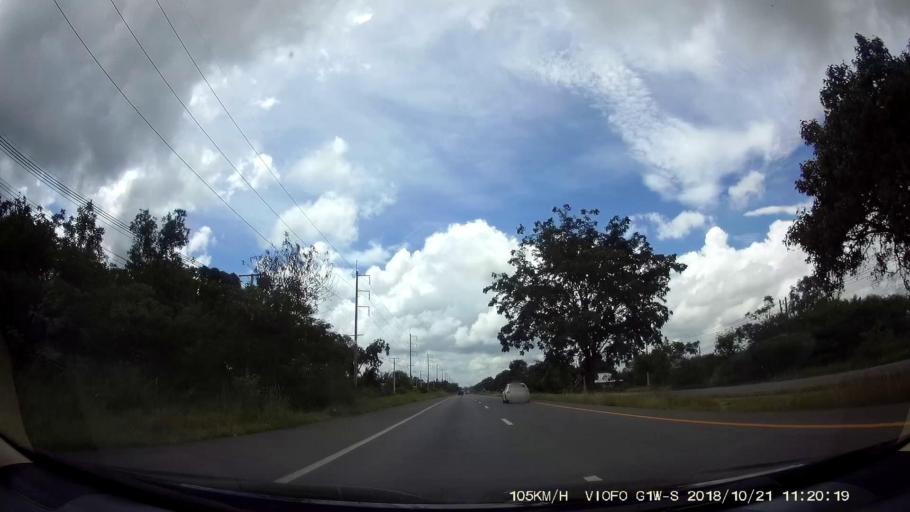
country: TH
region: Chaiyaphum
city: Chaiyaphum
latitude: 15.8580
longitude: 102.0763
